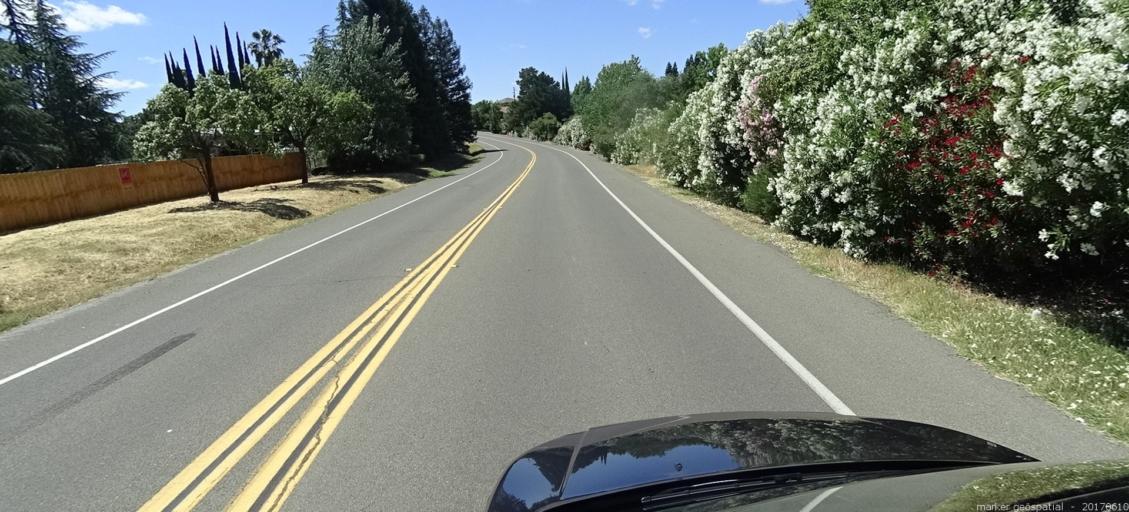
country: US
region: California
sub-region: Butte County
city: Oroville East
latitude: 39.5224
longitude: -121.4668
